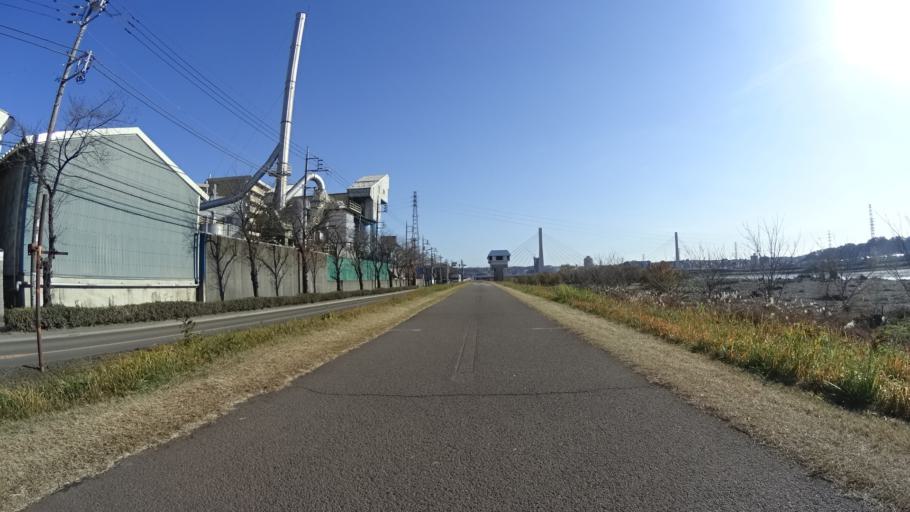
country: JP
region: Tokyo
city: Hino
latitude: 35.6650
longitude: 139.4369
